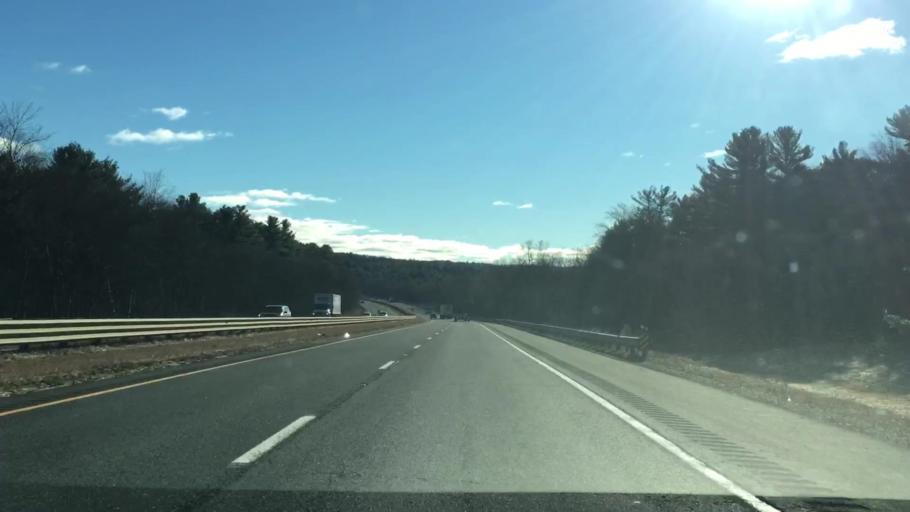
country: US
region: Massachusetts
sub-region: Worcester County
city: Fiskdale
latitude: 42.1397
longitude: -72.1341
